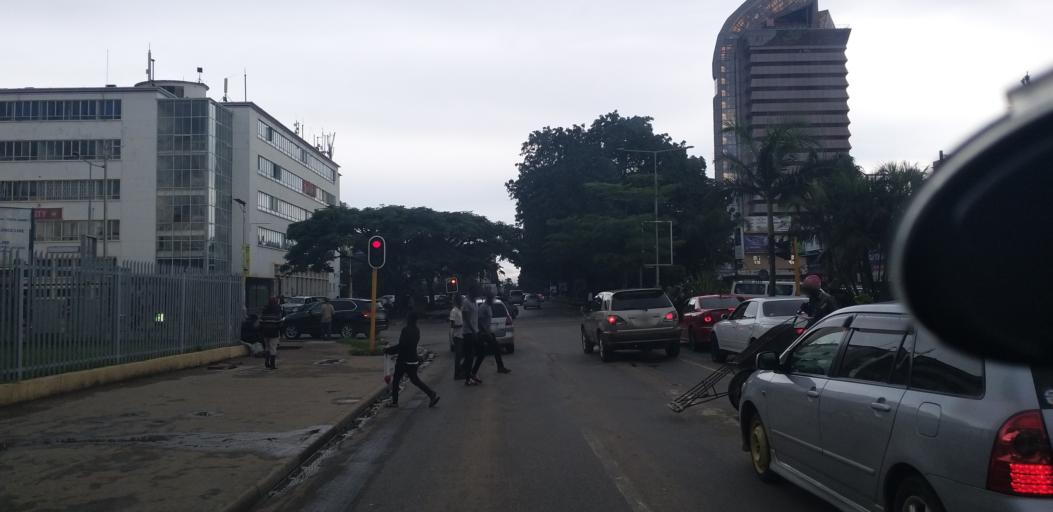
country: ZM
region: Lusaka
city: Lusaka
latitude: -15.4158
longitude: 28.2817
